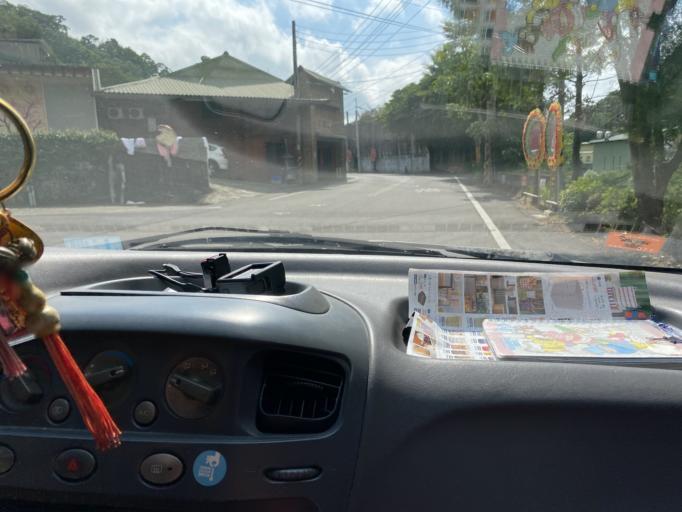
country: TW
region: Taiwan
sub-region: Hsinchu
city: Zhubei
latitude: 24.7416
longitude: 121.1344
